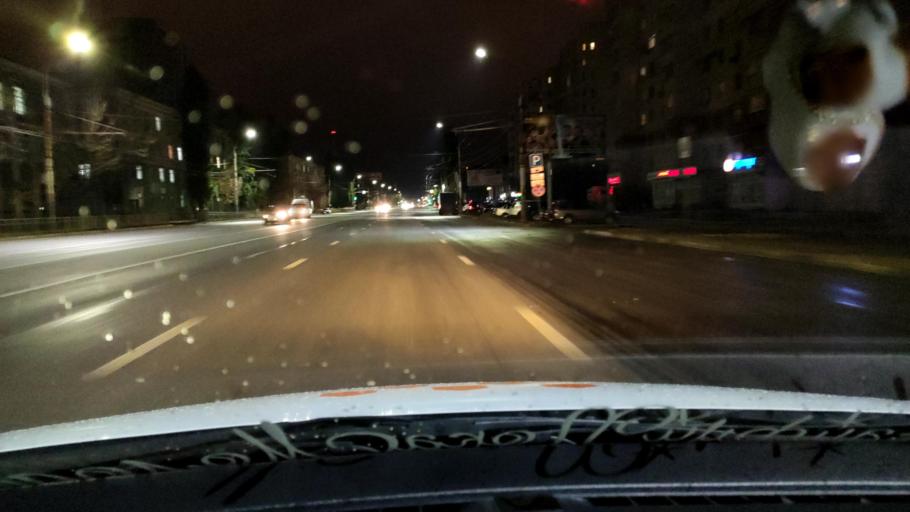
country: RU
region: Voronezj
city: Voronezh
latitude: 51.6473
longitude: 39.1968
